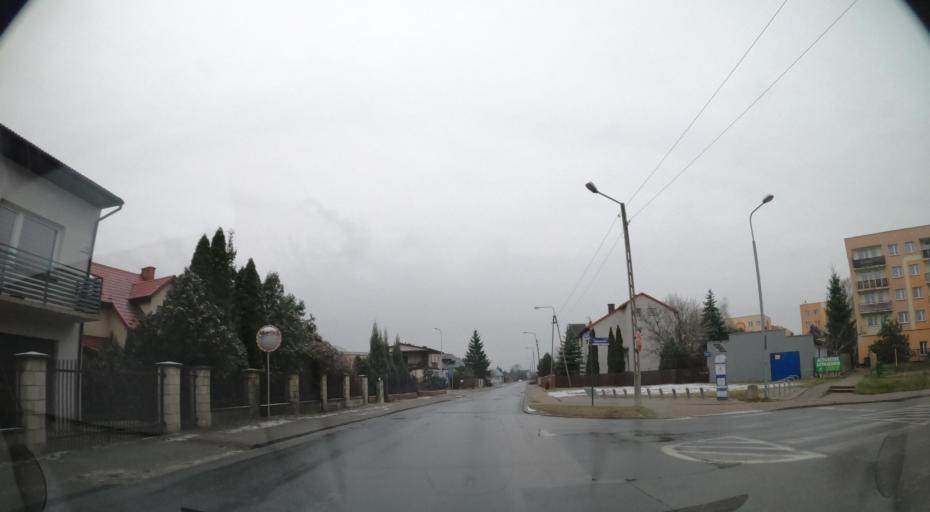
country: PL
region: Masovian Voivodeship
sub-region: Powiat radomski
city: Trablice
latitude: 51.3835
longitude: 21.1086
